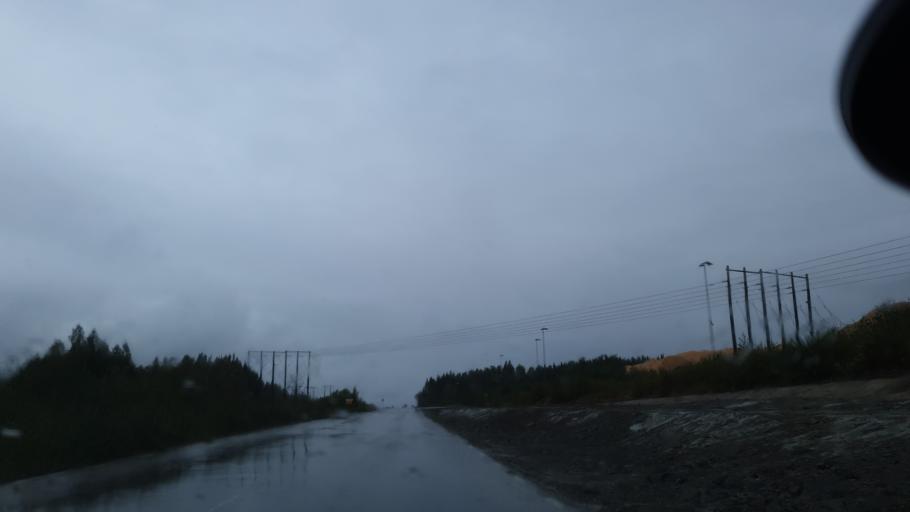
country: SE
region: Vaesterbotten
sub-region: Skelleftea Kommun
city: Soedra Bergsbyn
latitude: 64.7433
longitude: 21.0638
